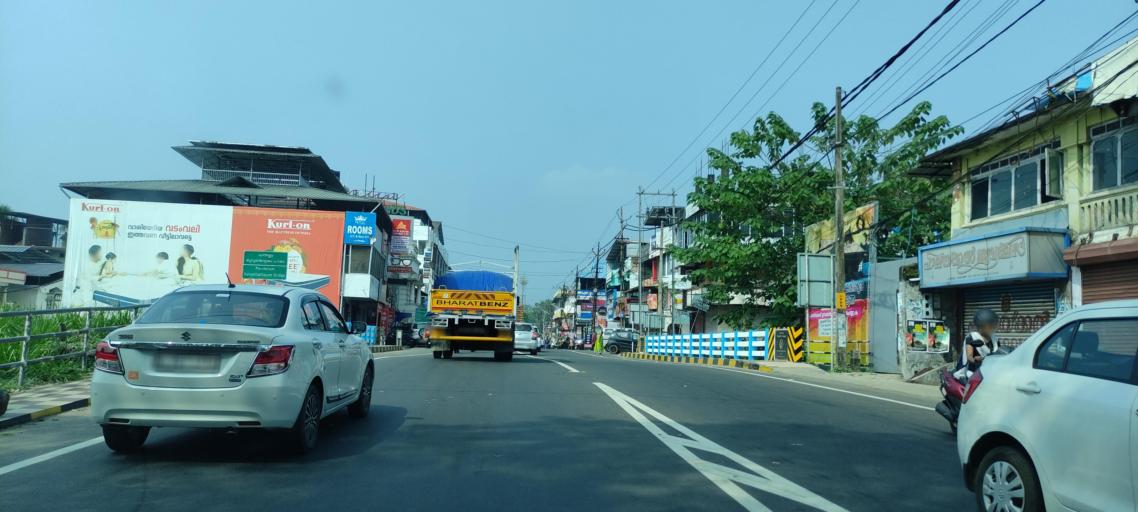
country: IN
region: Kerala
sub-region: Pattanamtitta
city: Adur
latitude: 9.2253
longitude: 76.6784
